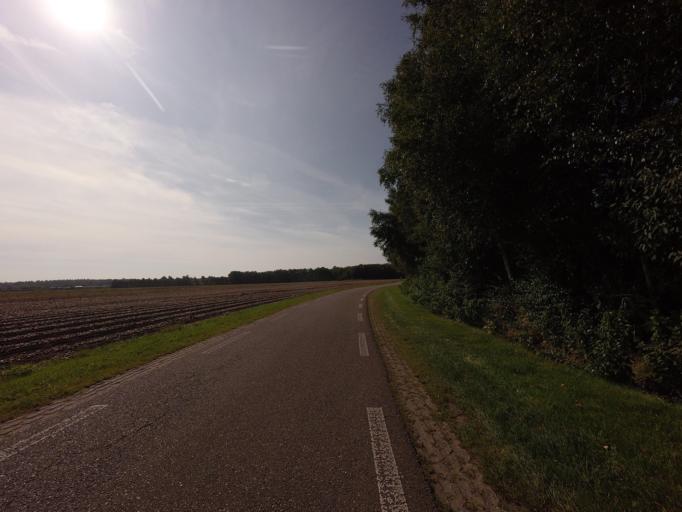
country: NL
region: Drenthe
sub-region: Gemeente Borger-Odoorn
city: Borger
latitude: 52.9171
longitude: 6.7106
